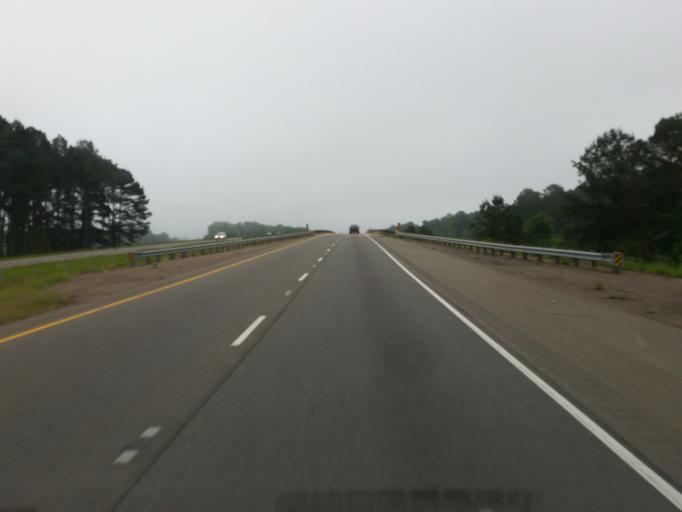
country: US
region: Louisiana
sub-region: Webster Parish
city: Sibley
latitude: 32.5824
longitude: -93.3941
